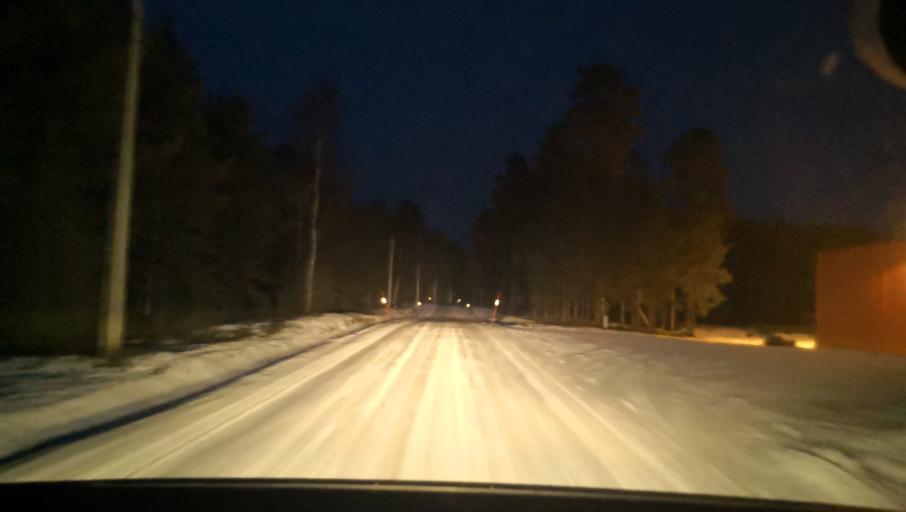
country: SE
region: Uppsala
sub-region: Heby Kommun
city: Tarnsjo
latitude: 60.2700
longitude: 16.7947
